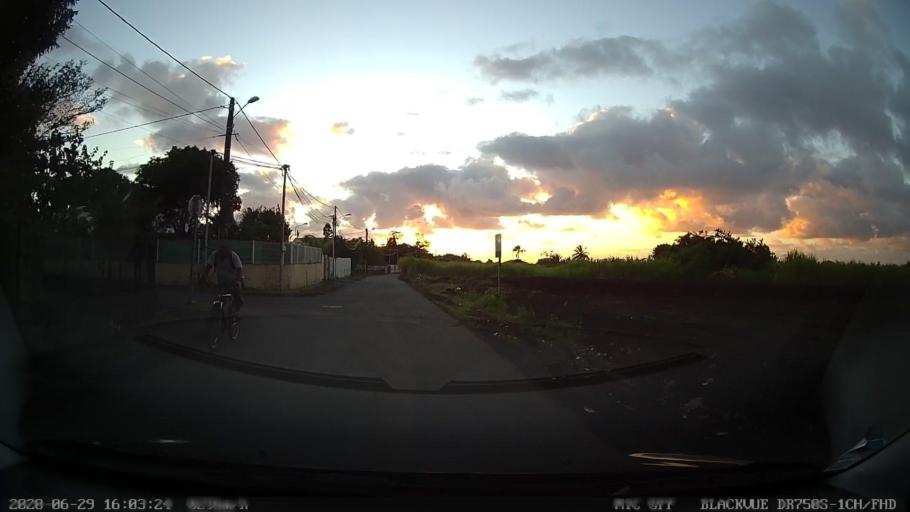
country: RE
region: Reunion
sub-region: Reunion
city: Bras-Panon
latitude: -20.9923
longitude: 55.6805
